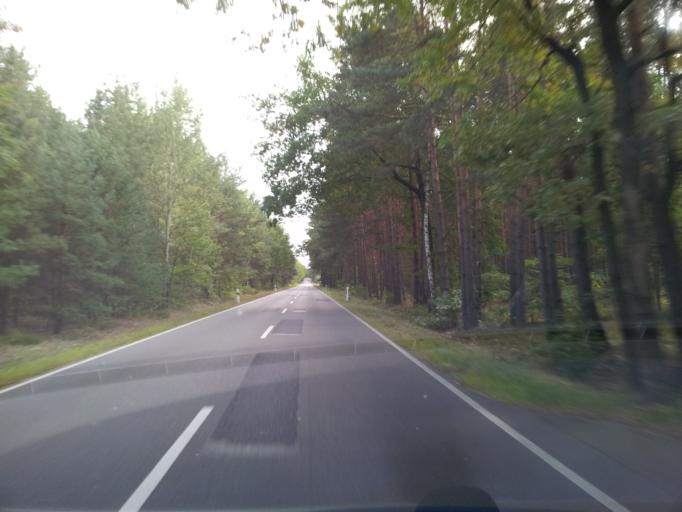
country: DE
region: Brandenburg
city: Finsterwalde
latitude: 51.6074
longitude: 13.7694
